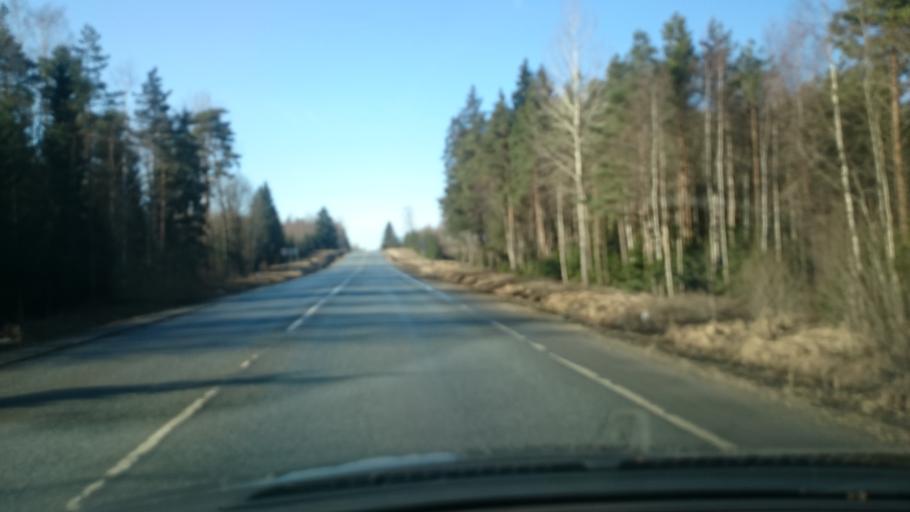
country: EE
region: Raplamaa
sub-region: Rapla vald
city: Rapla
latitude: 59.0378
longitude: 24.8334
